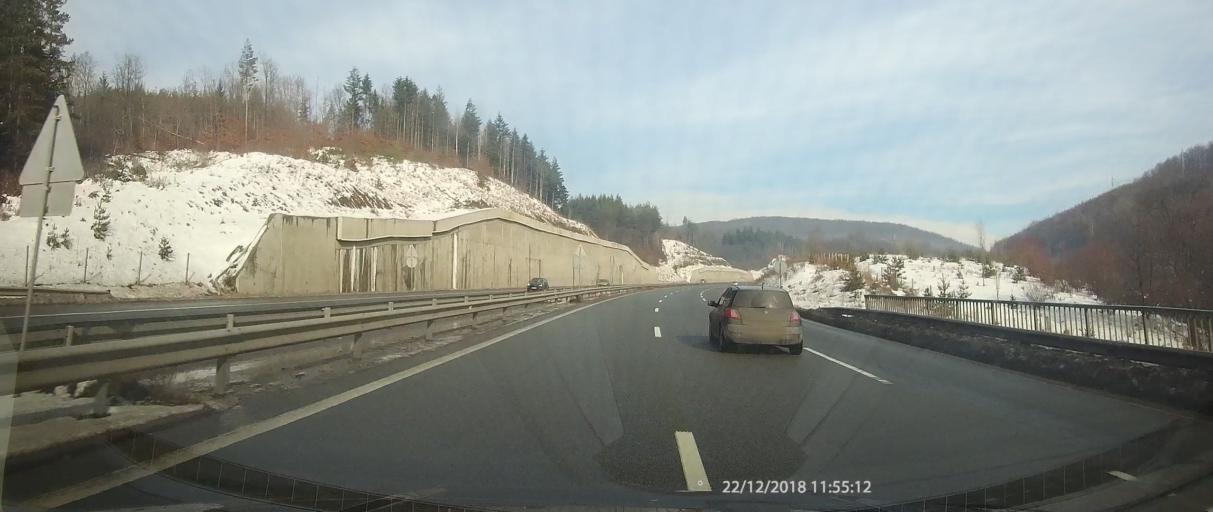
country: BG
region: Pernik
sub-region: Obshtina Pernik
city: Pernik
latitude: 42.6549
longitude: 23.1306
